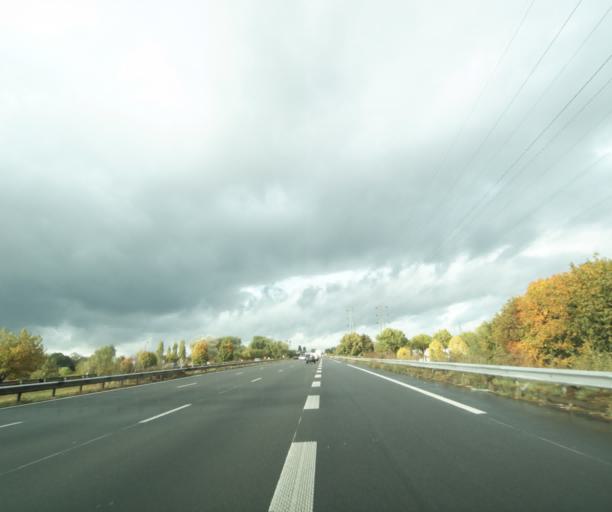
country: FR
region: Nord-Pas-de-Calais
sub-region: Departement du Nord
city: Wasquehal
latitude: 50.6780
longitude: 3.1134
